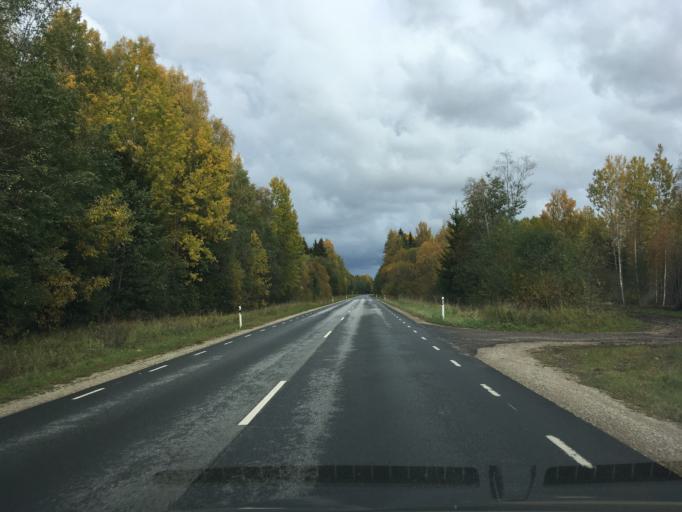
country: EE
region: Harju
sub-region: Anija vald
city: Kehra
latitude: 59.2672
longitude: 25.3545
